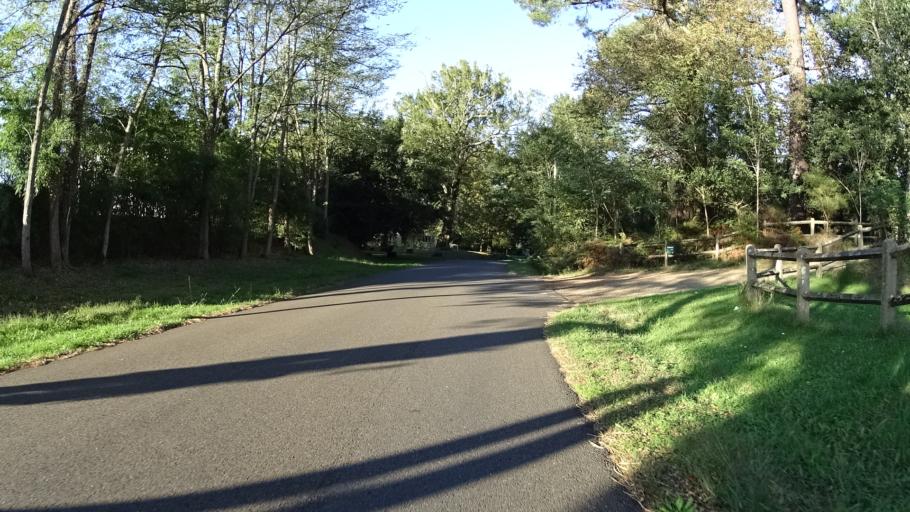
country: FR
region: Aquitaine
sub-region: Departement des Landes
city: Saint-Paul-les-Dax
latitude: 43.7347
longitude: -1.0441
